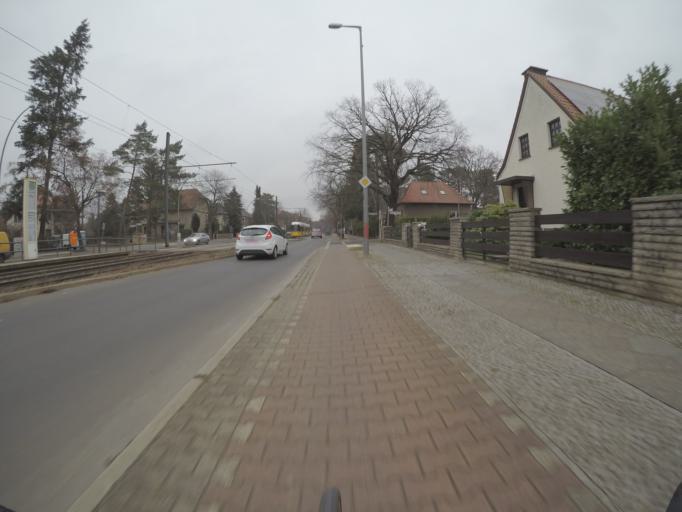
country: DE
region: Berlin
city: Kopenick Bezirk
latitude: 52.4673
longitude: 13.5859
